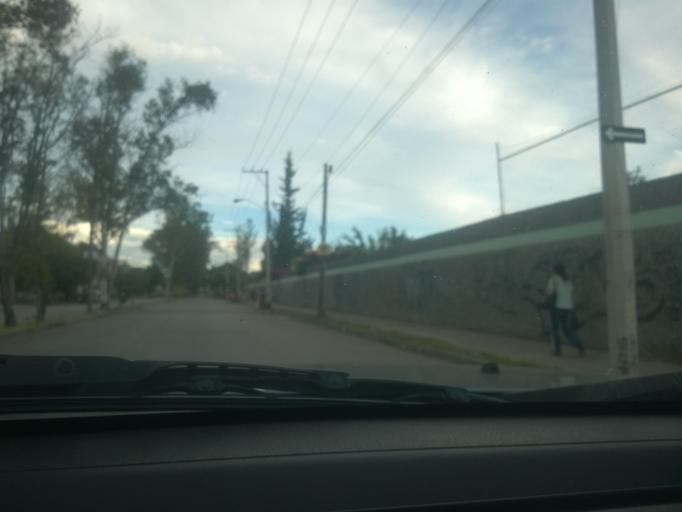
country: MX
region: Guanajuato
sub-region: Leon
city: Medina
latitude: 21.1302
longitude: -101.6400
